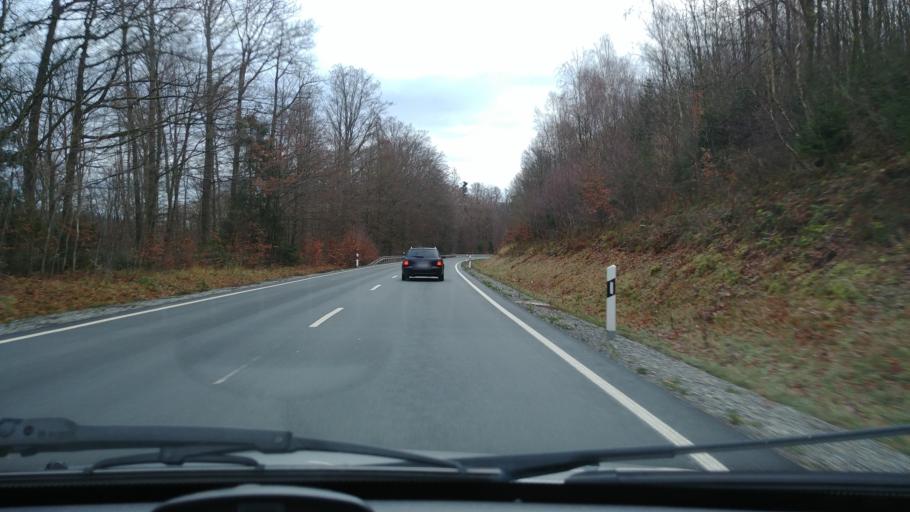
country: DE
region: Bavaria
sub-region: Regierungsbezirk Unterfranken
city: Neuhutten
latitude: 49.9845
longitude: 9.4073
